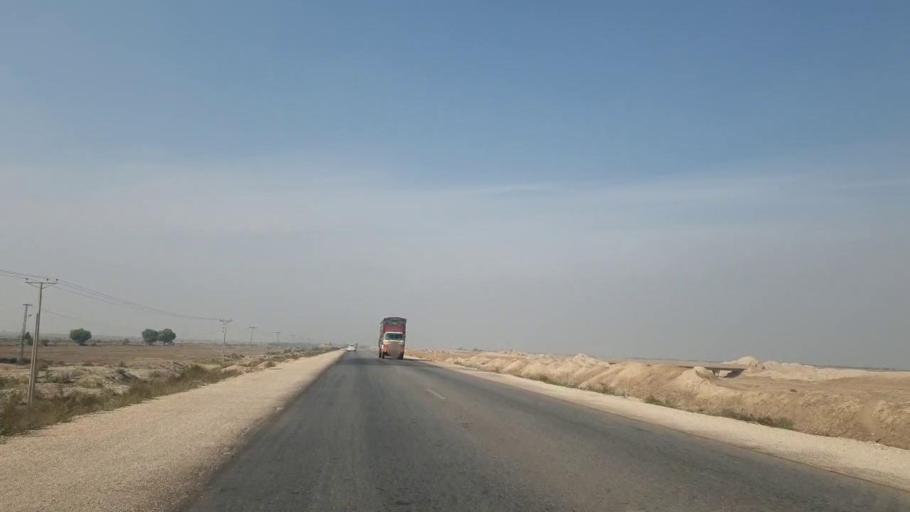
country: PK
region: Sindh
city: Sann
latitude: 25.9219
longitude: 68.2162
